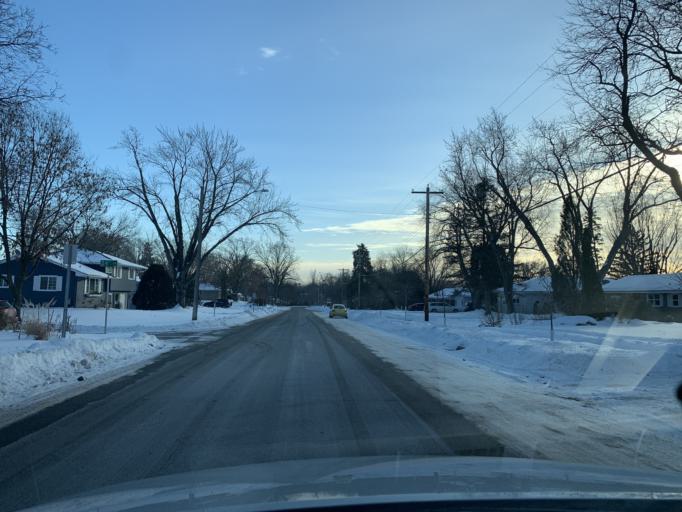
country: US
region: Minnesota
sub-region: Hennepin County
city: Minnetonka Mills
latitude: 44.9579
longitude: -93.3962
